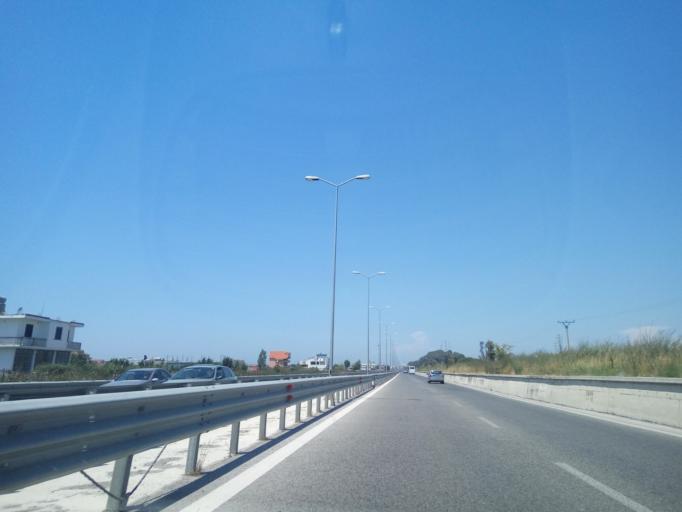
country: AL
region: Tirane
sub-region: Rrethi i Kavajes
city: Golem
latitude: 41.2155
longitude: 19.5310
